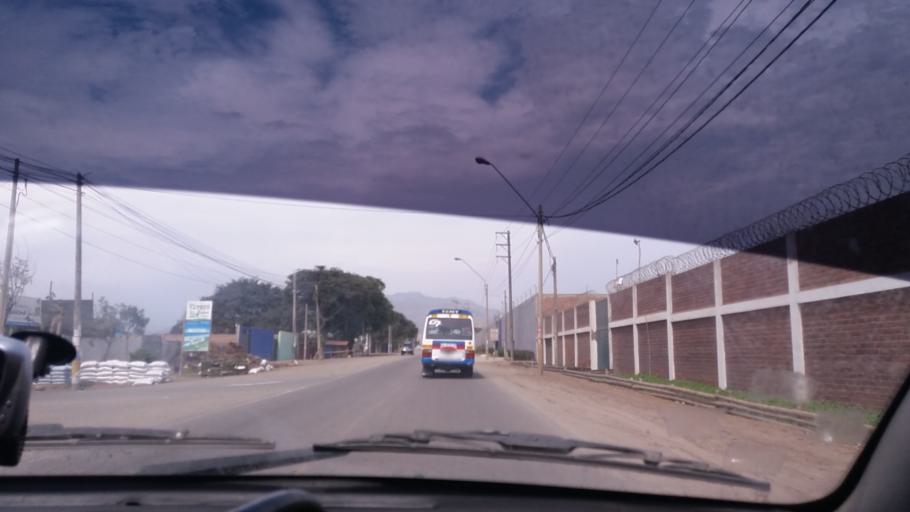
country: PE
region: Lima
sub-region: Lima
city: Punta Hermosa
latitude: -12.2556
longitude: -76.8793
